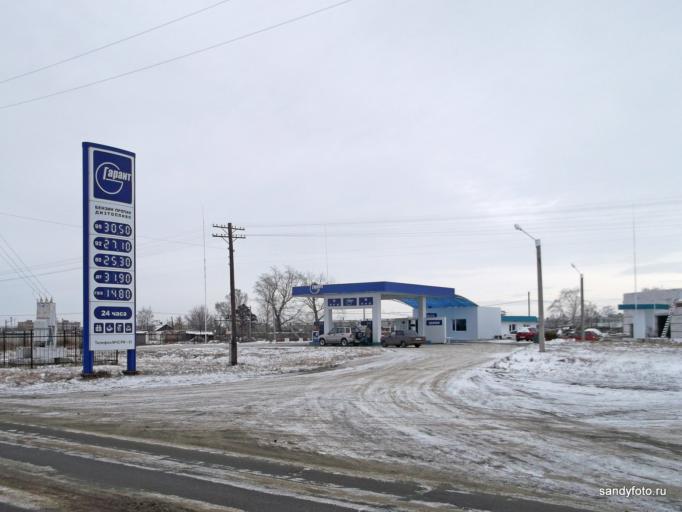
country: RU
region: Chelyabinsk
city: Troitsk
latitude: 54.0839
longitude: 61.5202
